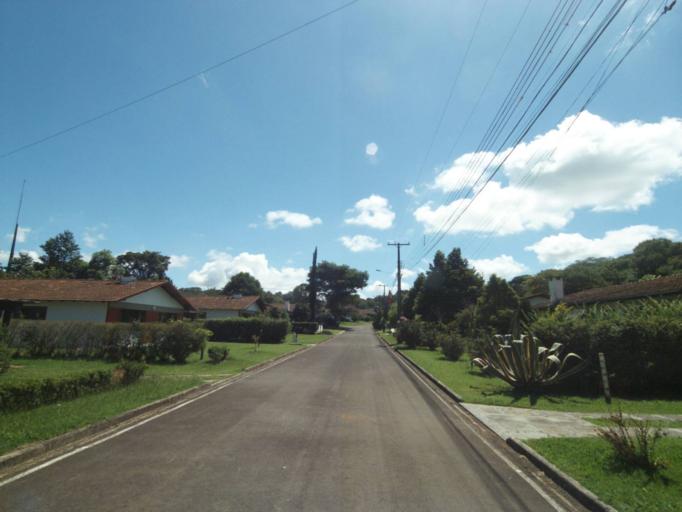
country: BR
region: Parana
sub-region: Chopinzinho
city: Chopinzinho
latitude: -25.7989
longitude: -52.0963
